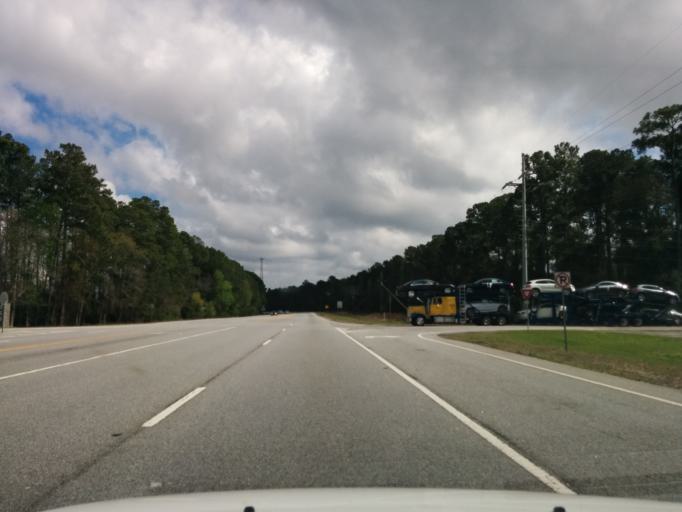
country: US
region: Georgia
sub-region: Glynn County
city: Brunswick
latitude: 31.1177
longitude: -81.5398
